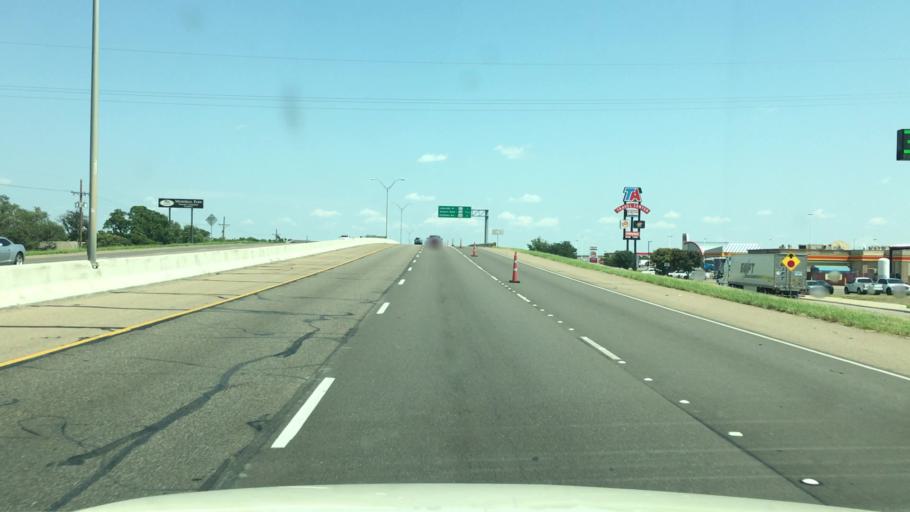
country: US
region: Texas
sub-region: Potter County
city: Amarillo
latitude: 35.1926
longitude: -101.7626
